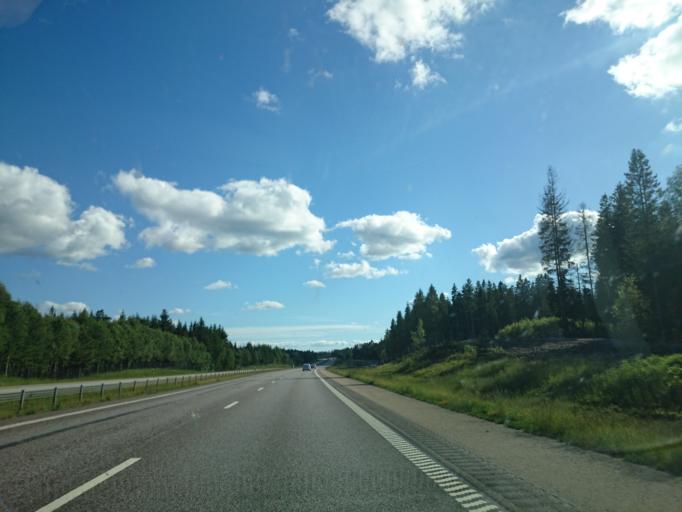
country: SE
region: Kronoberg
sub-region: Markaryds Kommun
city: Stromsnasbruk
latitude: 56.5943
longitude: 13.7352
